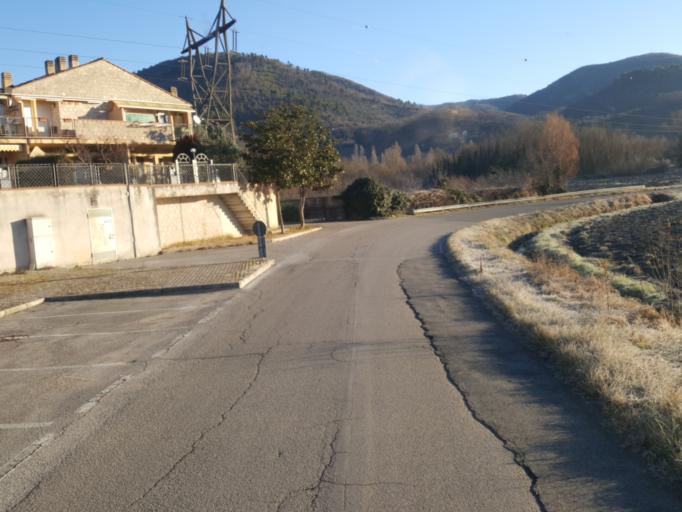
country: IT
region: Latium
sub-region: Provincia di Rieti
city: Labro
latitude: 42.5373
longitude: 12.7691
